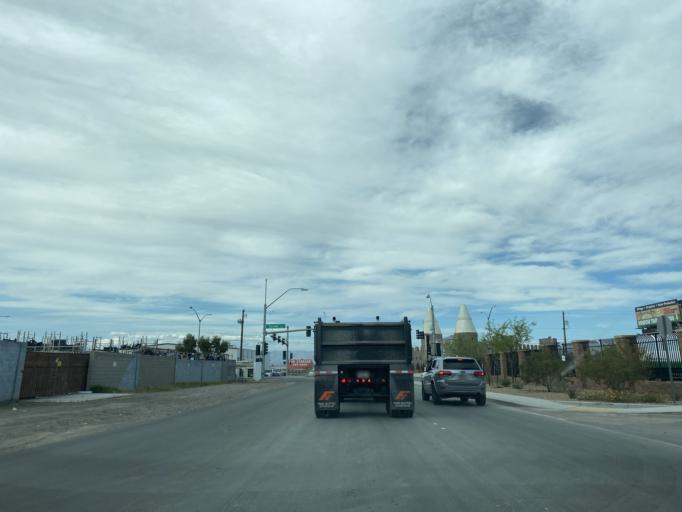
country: US
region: Nevada
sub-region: Clark County
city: Henderson
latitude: 36.0631
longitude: -115.0202
